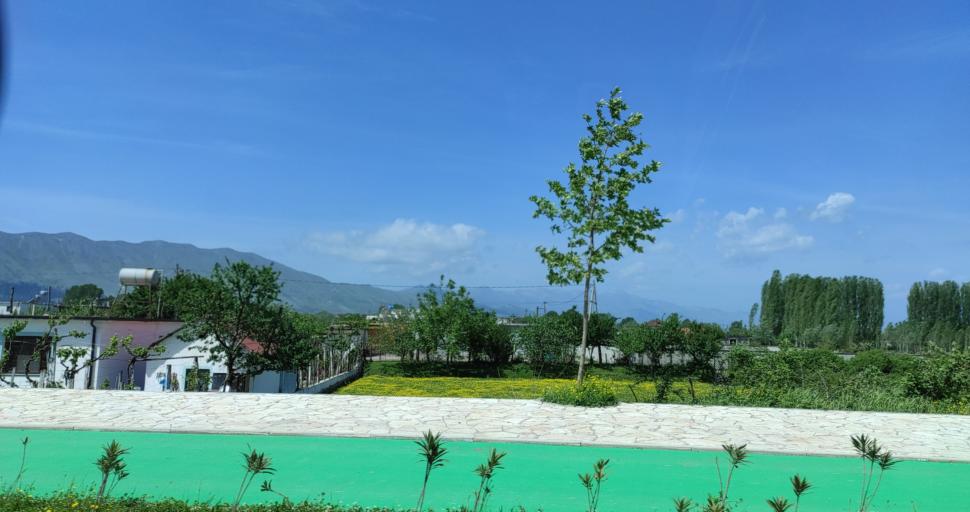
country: AL
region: Shkoder
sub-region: Rrethi i Shkodres
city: Shkoder
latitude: 42.0791
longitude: 19.4922
